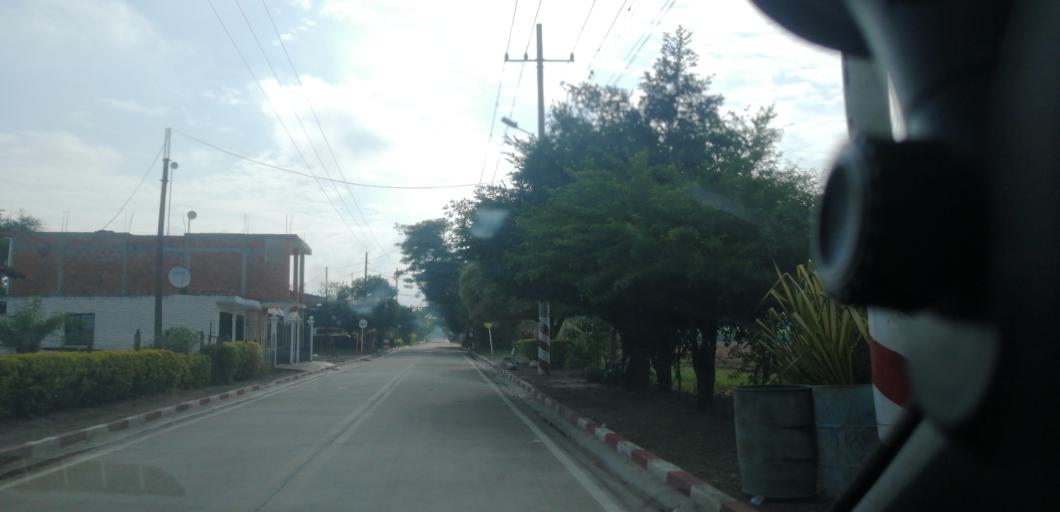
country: CO
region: Valle del Cauca
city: Yumbo
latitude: 3.5738
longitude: -76.4042
